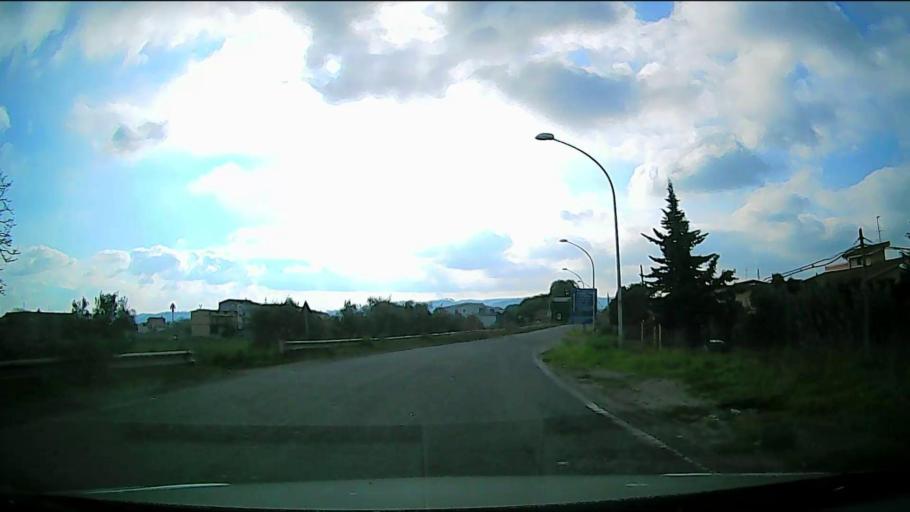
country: IT
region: Calabria
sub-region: Provincia di Crotone
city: Rocca di Neto
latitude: 39.1791
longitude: 17.0174
